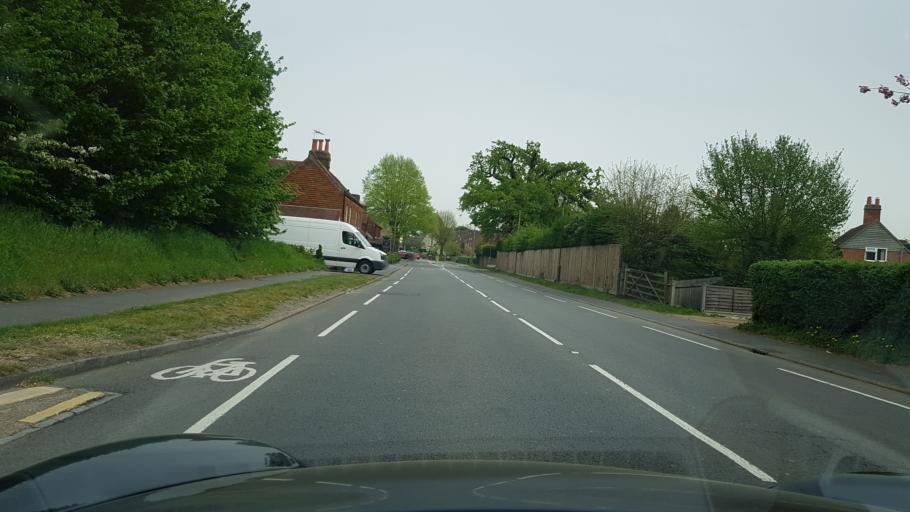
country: GB
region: England
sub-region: Surrey
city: Ripley
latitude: 51.2980
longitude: -0.4964
